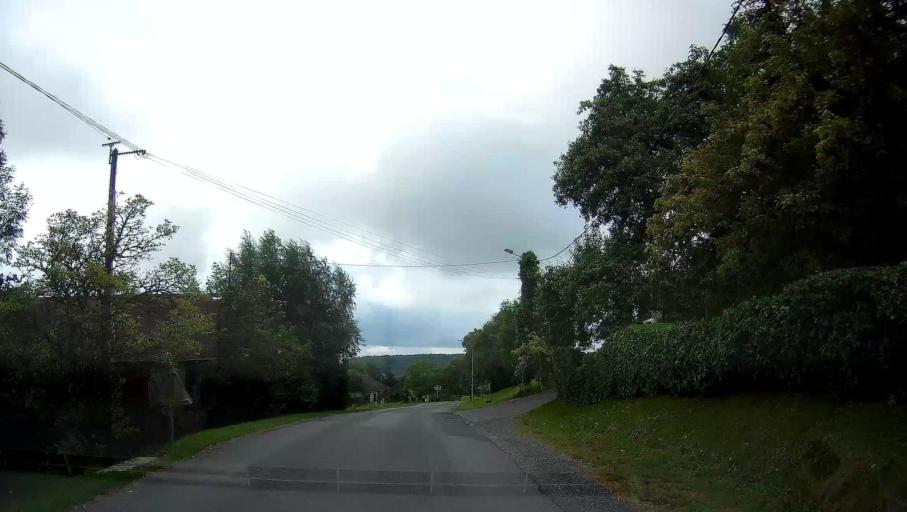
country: FR
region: Champagne-Ardenne
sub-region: Departement des Ardennes
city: Chateau-Porcien
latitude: 49.6470
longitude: 4.2493
